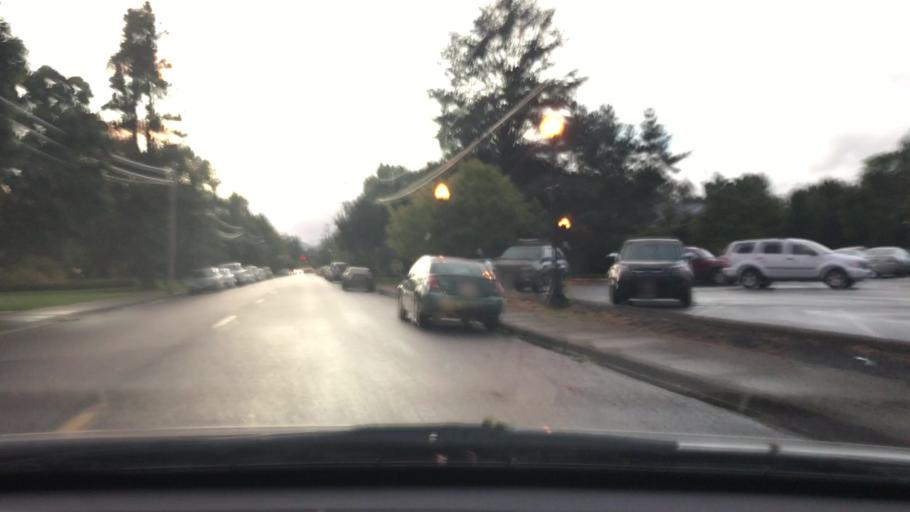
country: US
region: Oregon
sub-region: Yamhill County
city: McMinnville
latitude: 45.2003
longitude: -123.1955
